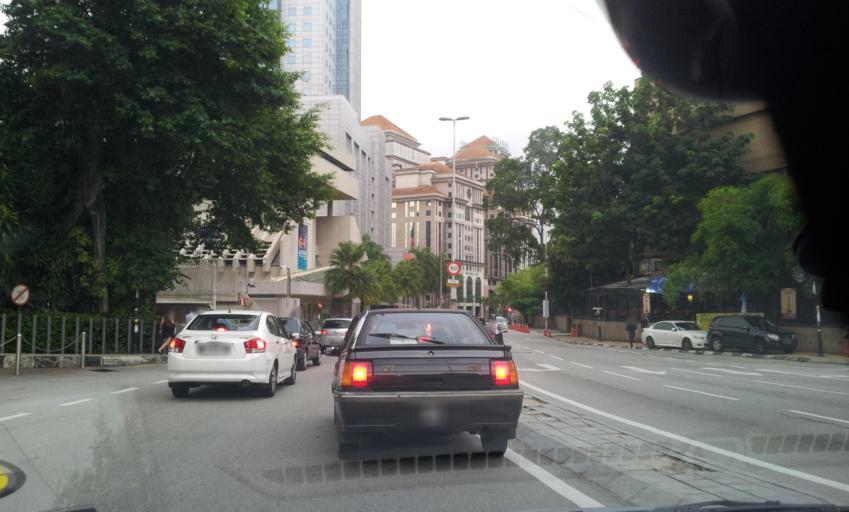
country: MY
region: Kuala Lumpur
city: Kuala Lumpur
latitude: 3.1596
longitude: 101.7104
